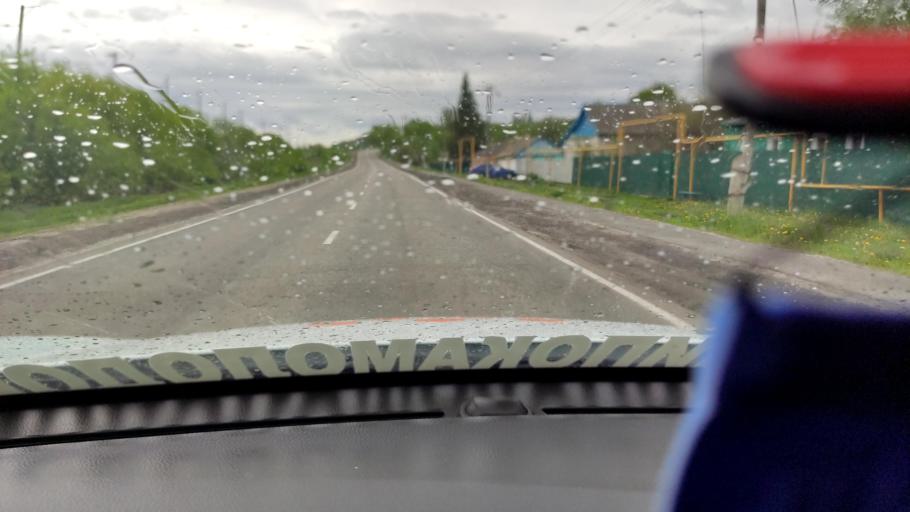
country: RU
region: Voronezj
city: Imeni Pervogo Maya
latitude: 50.7555
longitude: 39.3886
